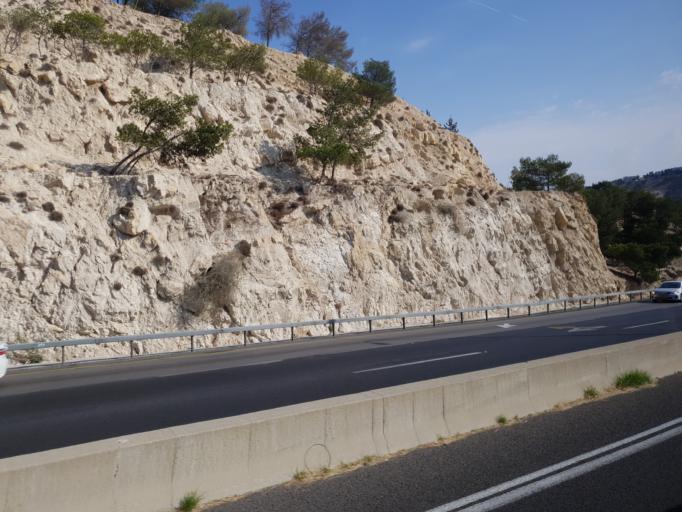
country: PS
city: Az Za`ayyim
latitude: 31.7840
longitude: 35.2824
